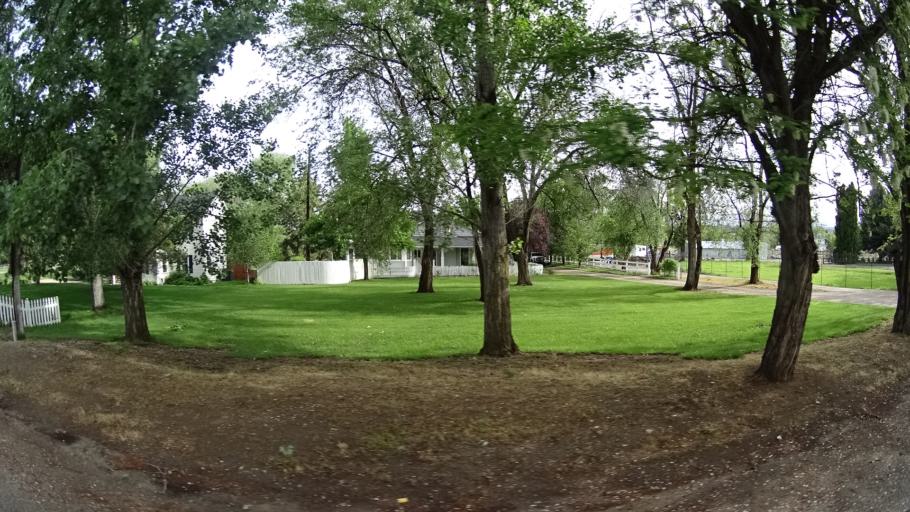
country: US
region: Idaho
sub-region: Ada County
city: Eagle
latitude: 43.7208
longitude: -116.3510
